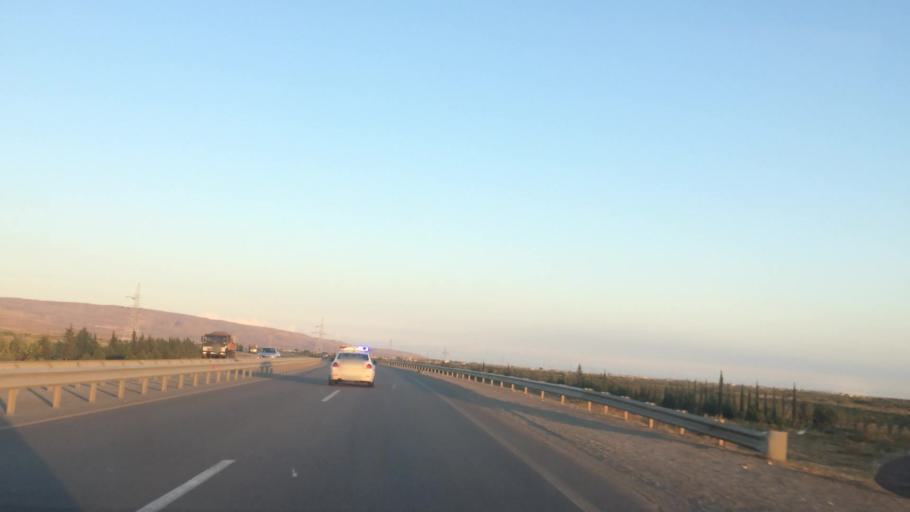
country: AZ
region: Baki
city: Qobustan
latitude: 39.9825
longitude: 49.2185
